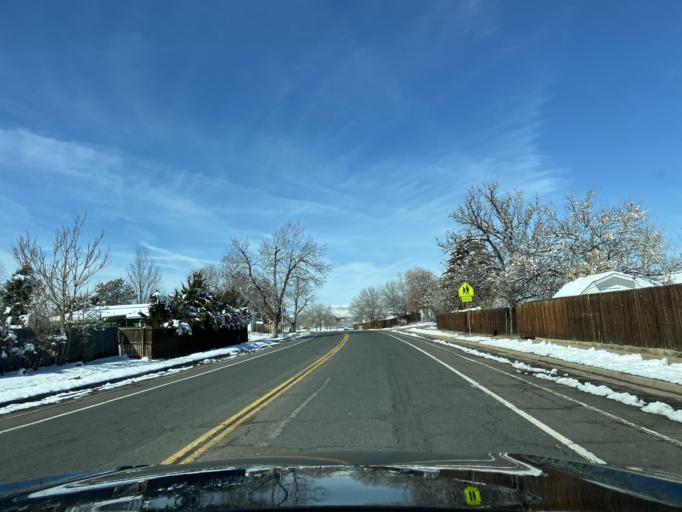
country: US
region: Colorado
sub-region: Adams County
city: Aurora
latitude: 39.7037
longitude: -104.8531
